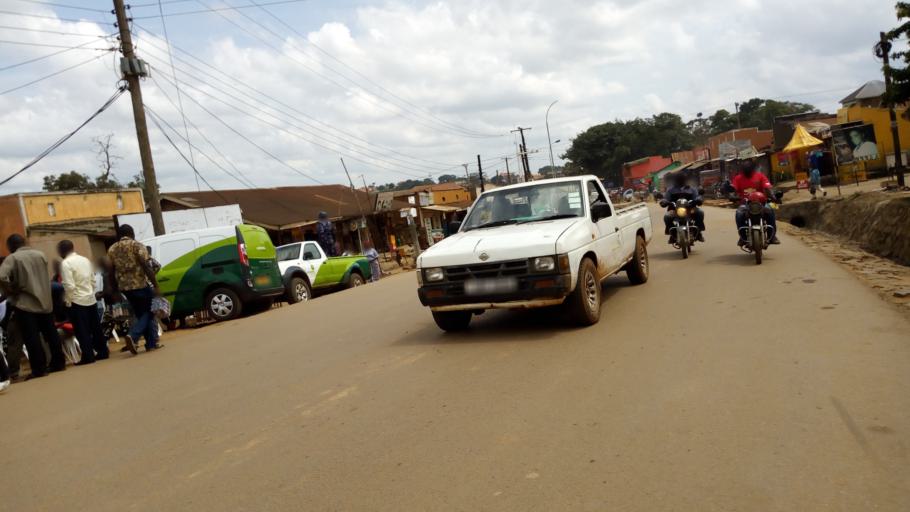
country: UG
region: Central Region
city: Kampala Central Division
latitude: 0.3802
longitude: 32.5582
